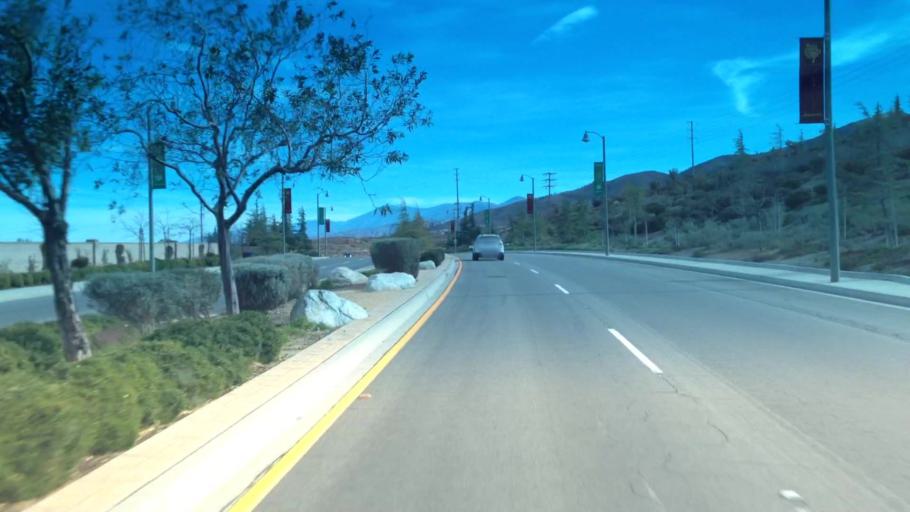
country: US
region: California
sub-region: Los Angeles County
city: Desert View Highlands
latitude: 34.5599
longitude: -118.1670
